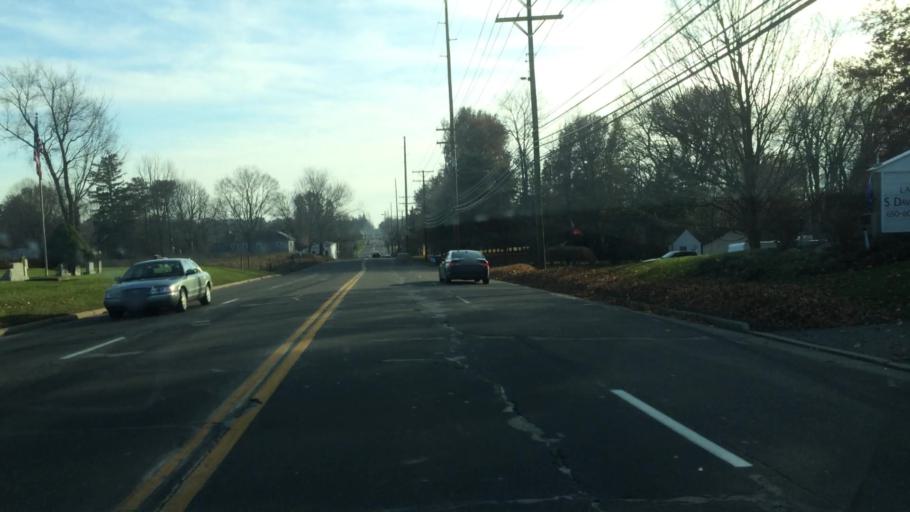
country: US
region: Ohio
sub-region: Summit County
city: Stow
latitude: 41.1994
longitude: -81.4405
